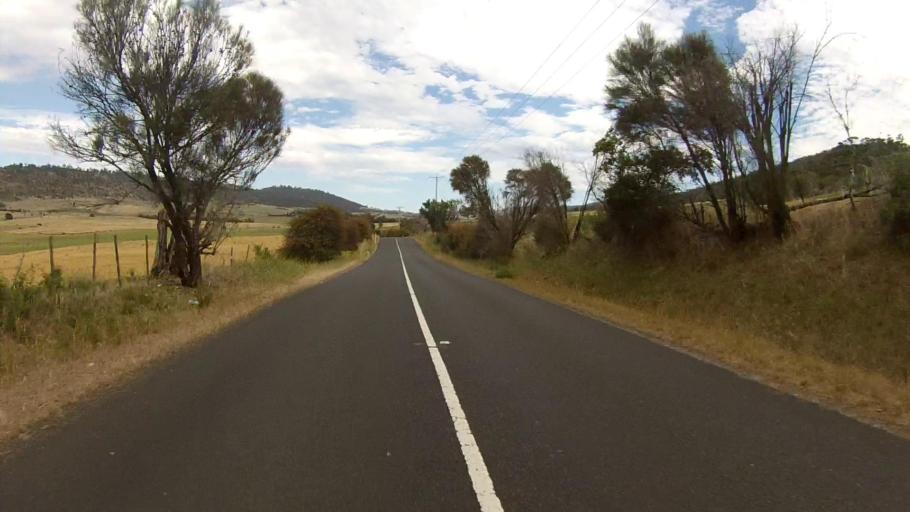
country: AU
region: Tasmania
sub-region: Clarence
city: Cambridge
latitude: -42.7332
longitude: 147.4083
